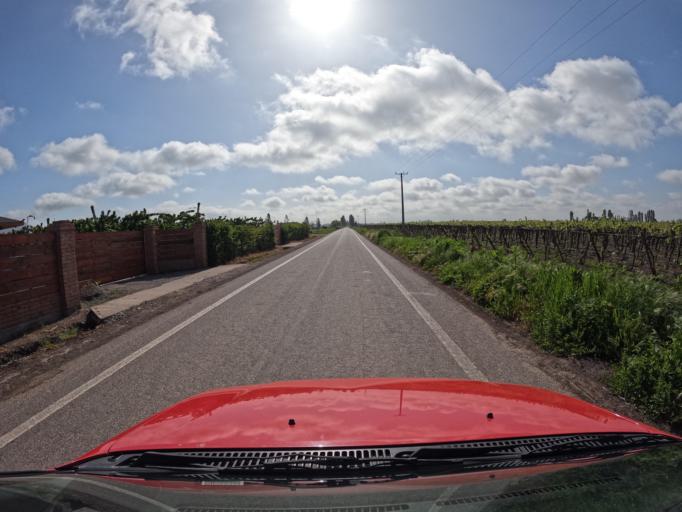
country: CL
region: Maule
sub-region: Provincia de Curico
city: Rauco
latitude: -34.8862
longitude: -71.2579
